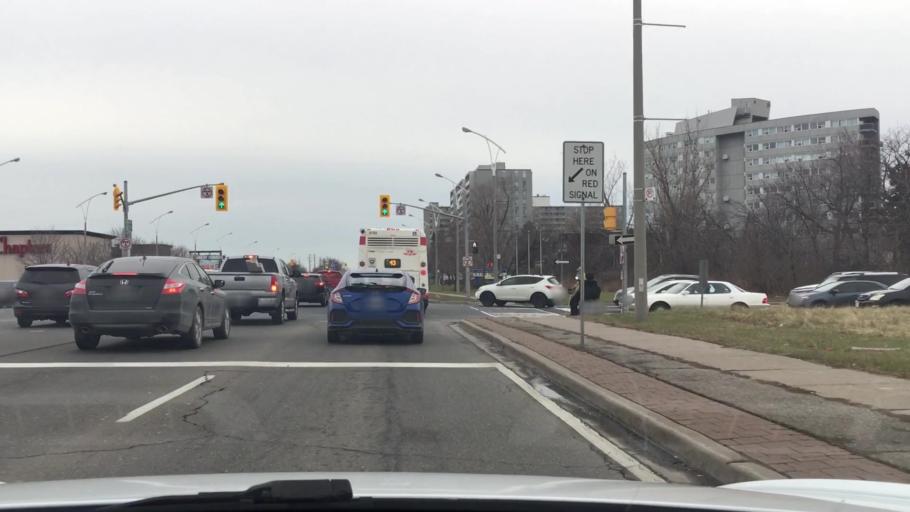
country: CA
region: Ontario
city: Scarborough
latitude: 43.7734
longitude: -79.2841
